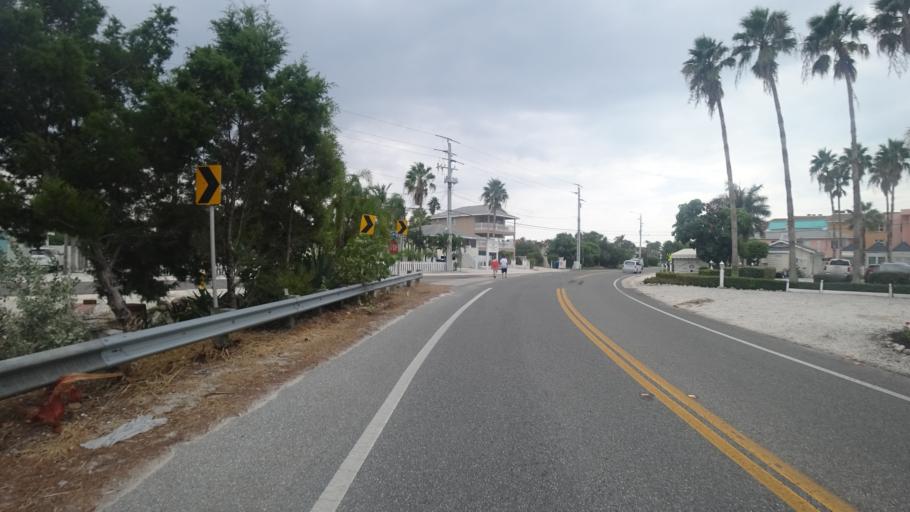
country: US
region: Florida
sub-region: Manatee County
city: Bradenton Beach
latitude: 27.4770
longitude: -82.7028
